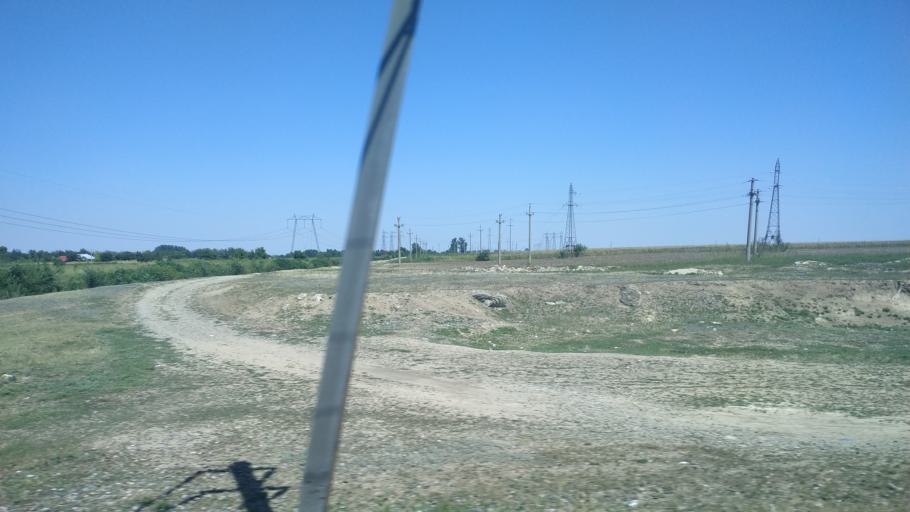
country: RO
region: Calarasi
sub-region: Comuna Perisoru
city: Perisoru
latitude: 44.4211
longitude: 27.6546
